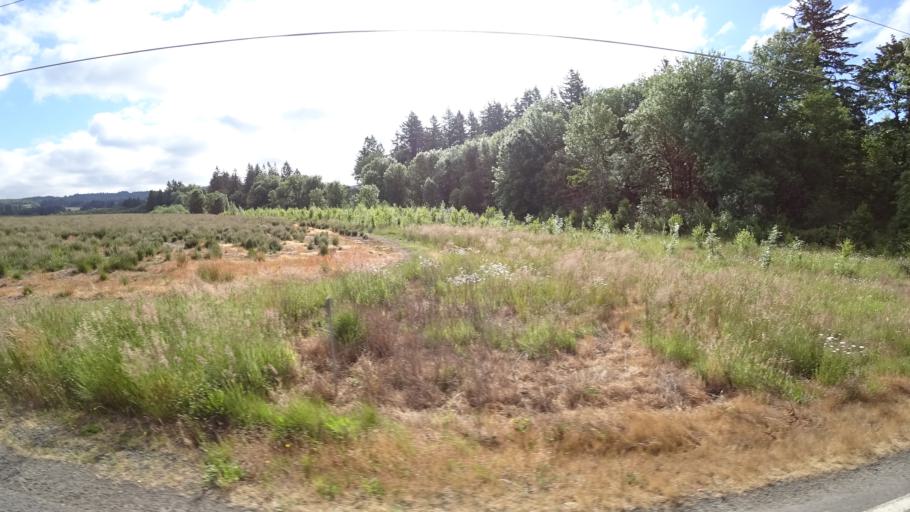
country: US
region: Oregon
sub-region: Washington County
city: Bethany
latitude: 45.5709
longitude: -122.8675
